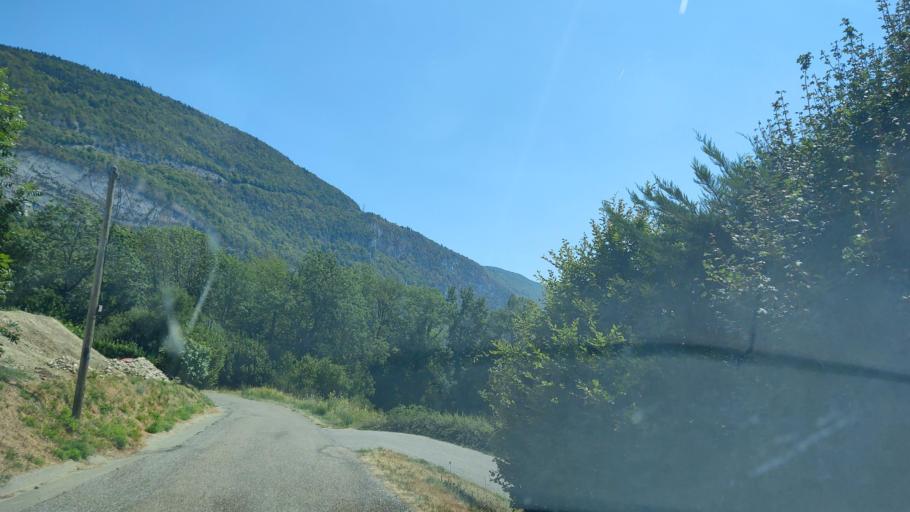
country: FR
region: Rhone-Alpes
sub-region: Departement de la Savoie
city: Novalaise
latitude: 45.5985
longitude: 5.7892
